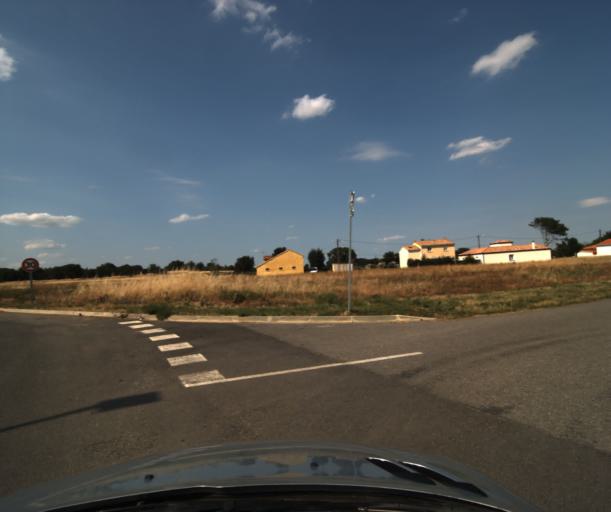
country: FR
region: Midi-Pyrenees
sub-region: Departement de la Haute-Garonne
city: Fonsorbes
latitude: 43.5278
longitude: 1.2094
